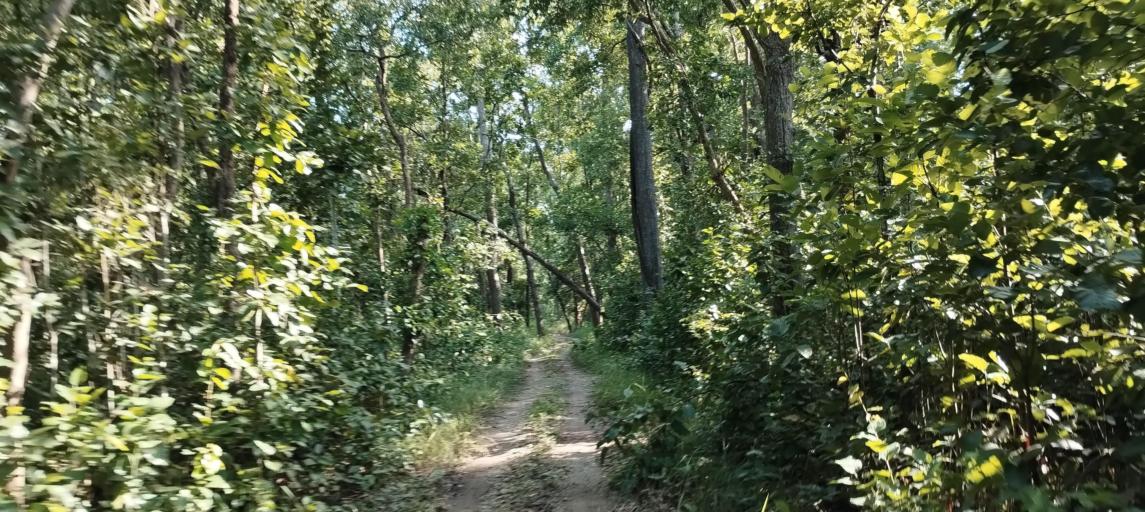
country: NP
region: Far Western
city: Tikapur
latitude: 28.5353
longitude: 81.2833
